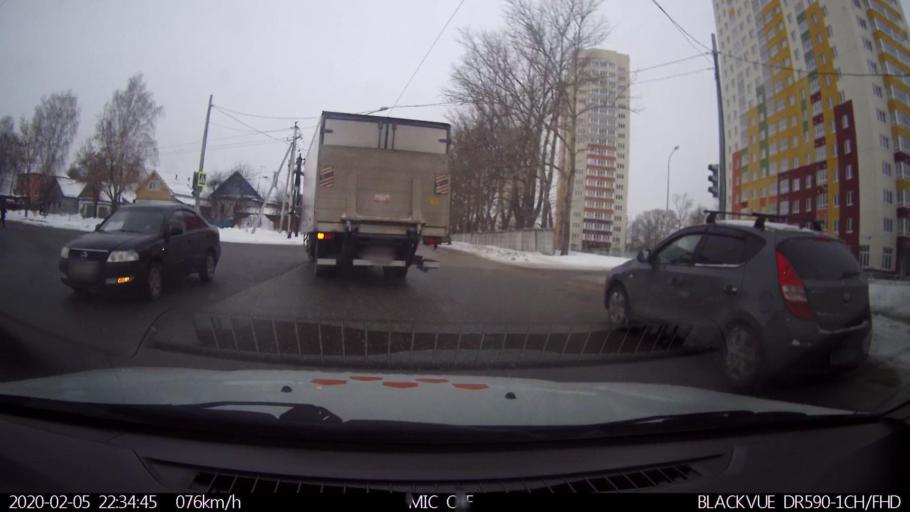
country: RU
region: Nizjnij Novgorod
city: Imeni Stepana Razina
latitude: 54.7351
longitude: 44.2286
